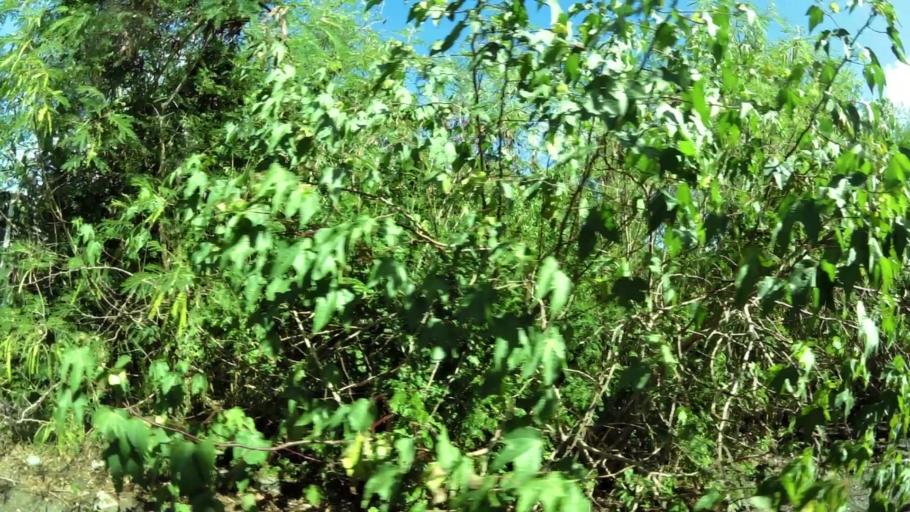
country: GP
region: Guadeloupe
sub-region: Guadeloupe
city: Port-Louis
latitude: 16.4138
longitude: -61.5262
